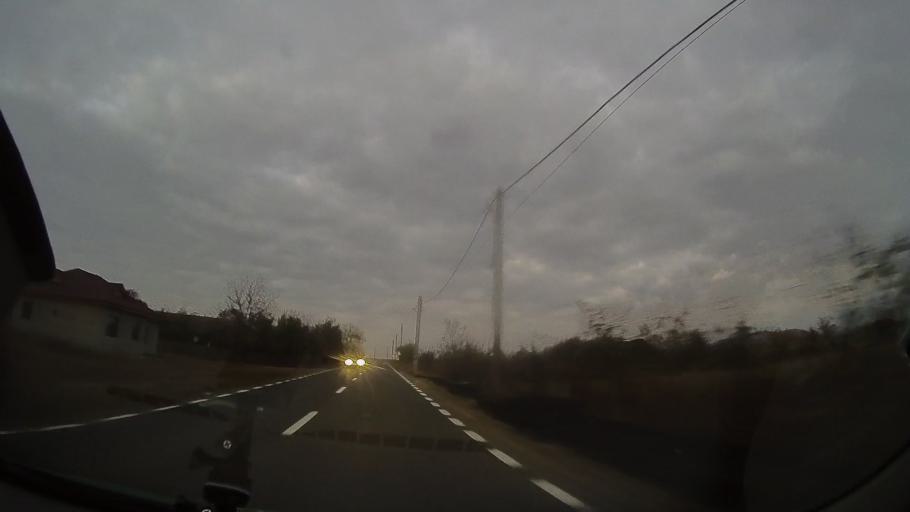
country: RO
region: Tulcea
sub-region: Comuna Nalbant
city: Nicolae Balcescu
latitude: 45.0005
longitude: 28.5935
